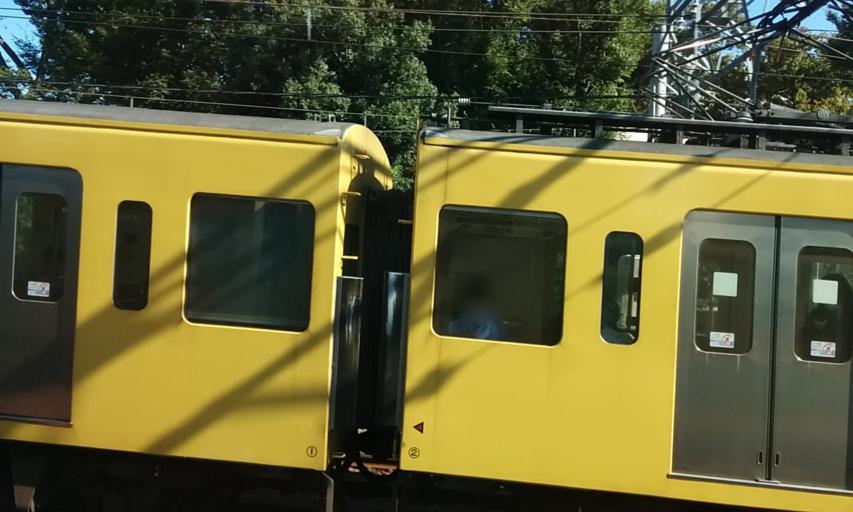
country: JP
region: Tokyo
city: Higashimurayama-shi
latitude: 35.7376
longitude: 139.4870
